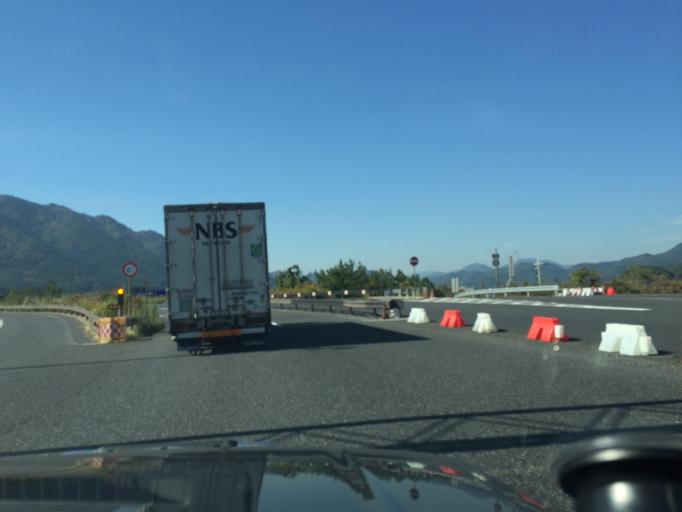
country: JP
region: Kyoto
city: Fukuchiyama
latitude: 35.1646
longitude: 135.1160
